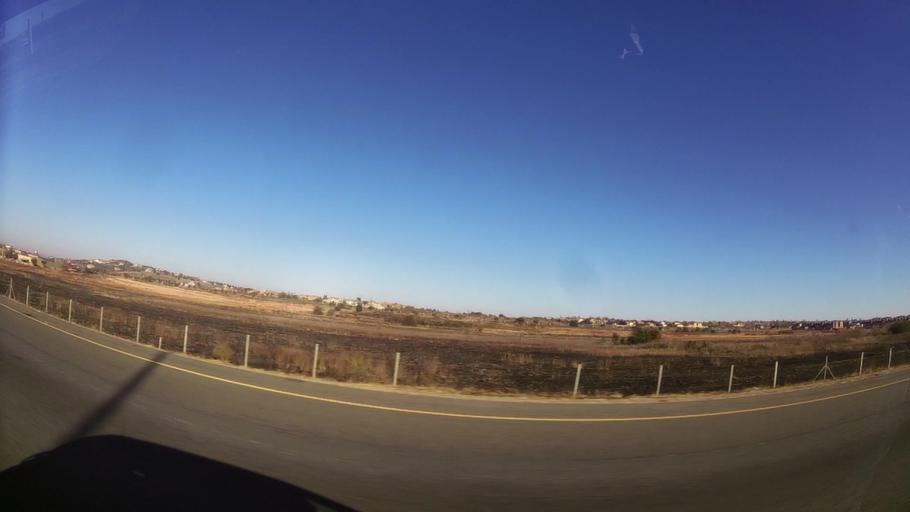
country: ZA
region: Gauteng
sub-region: City of Tshwane Metropolitan Municipality
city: Centurion
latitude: -25.8561
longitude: 28.2523
